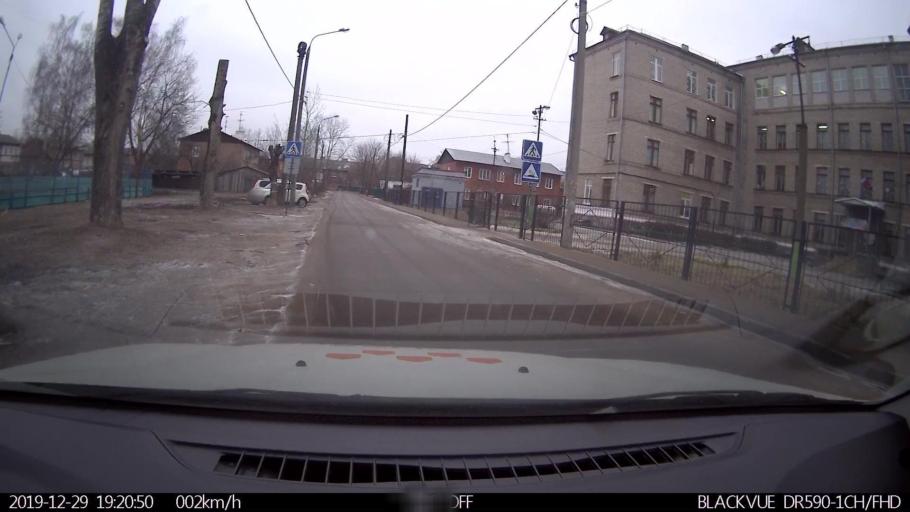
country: RU
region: Nizjnij Novgorod
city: Gorbatovka
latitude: 56.3818
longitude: 43.7903
